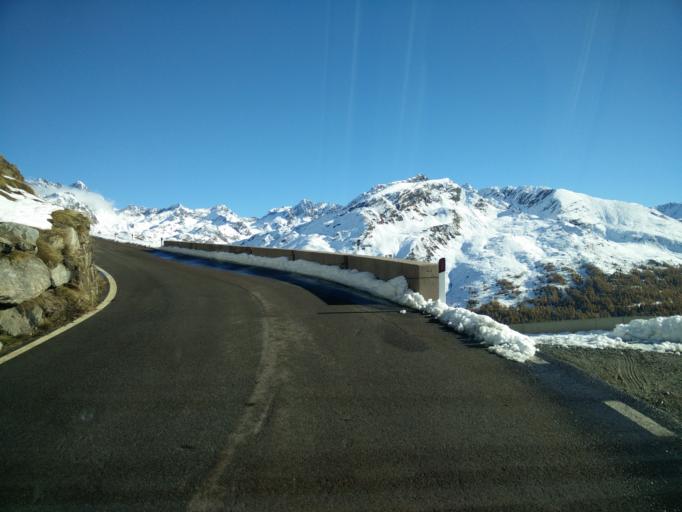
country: IT
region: Trentino-Alto Adige
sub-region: Bolzano
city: Moso in Passiria
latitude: 46.8892
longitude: 11.1198
